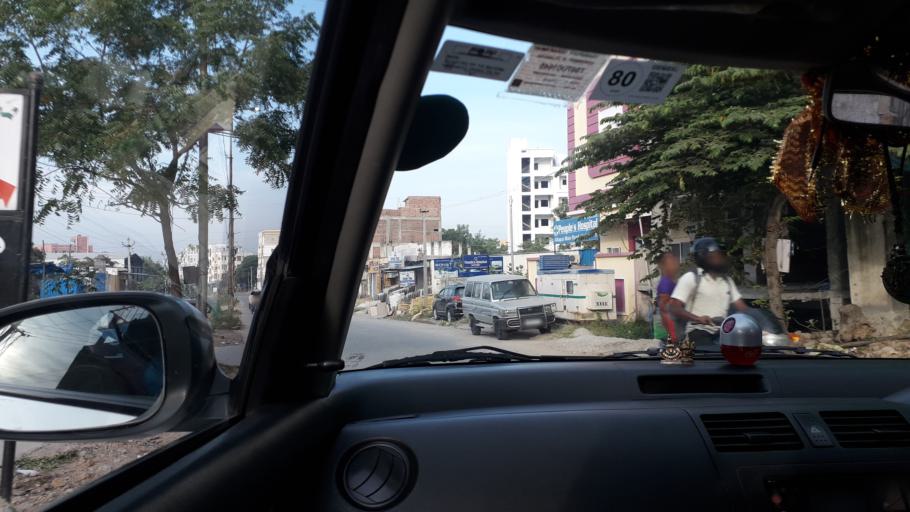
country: IN
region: Telangana
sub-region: Hyderabad
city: Hyderabad
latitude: 17.3949
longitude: 78.3841
